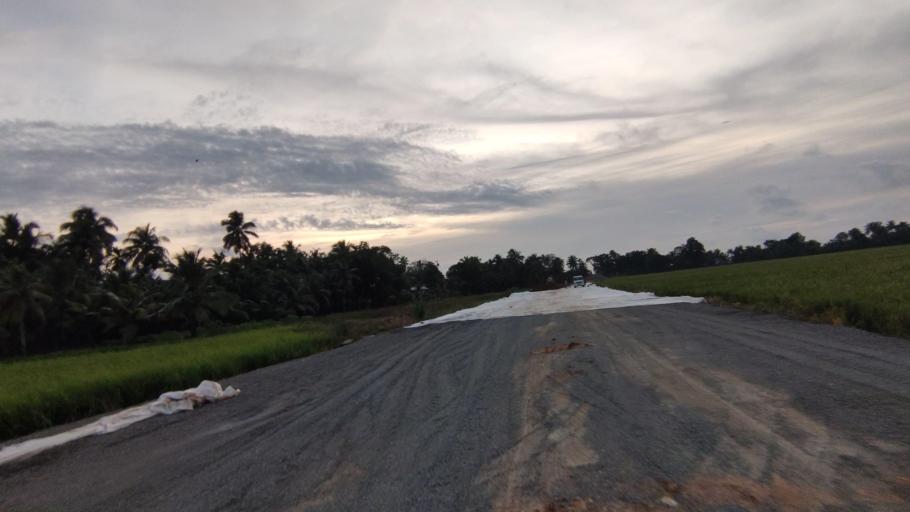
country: IN
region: Kerala
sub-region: Kottayam
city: Kottayam
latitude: 9.6470
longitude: 76.4676
